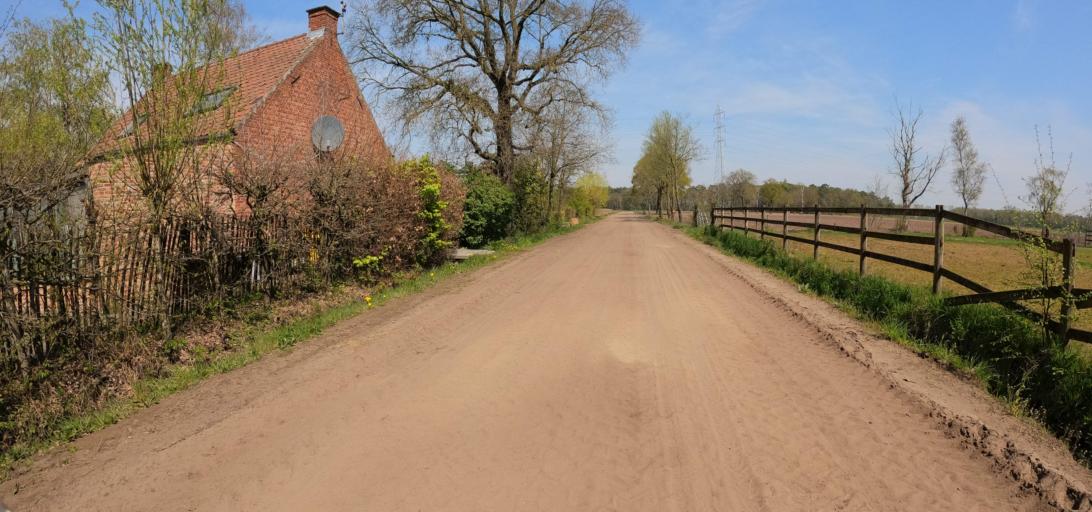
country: BE
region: Flanders
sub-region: Provincie Antwerpen
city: Vorselaar
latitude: 51.2325
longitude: 4.7765
